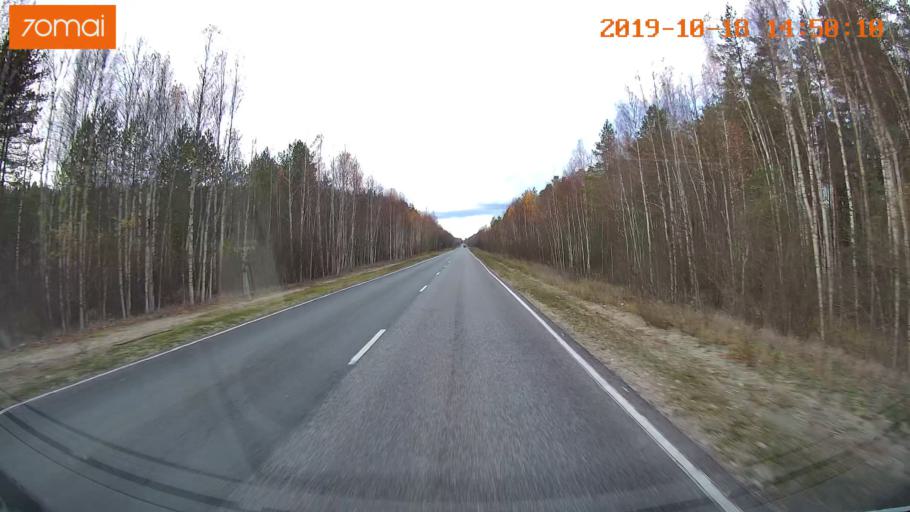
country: RU
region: Vladimir
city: Kurlovo
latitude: 55.4235
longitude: 40.6451
